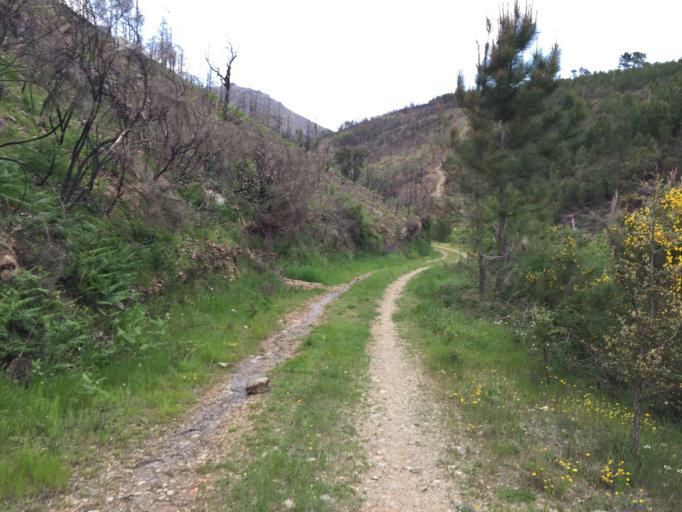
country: PT
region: Coimbra
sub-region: Pampilhosa da Serra
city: Pampilhosa da Serra
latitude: 40.1001
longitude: -7.8650
